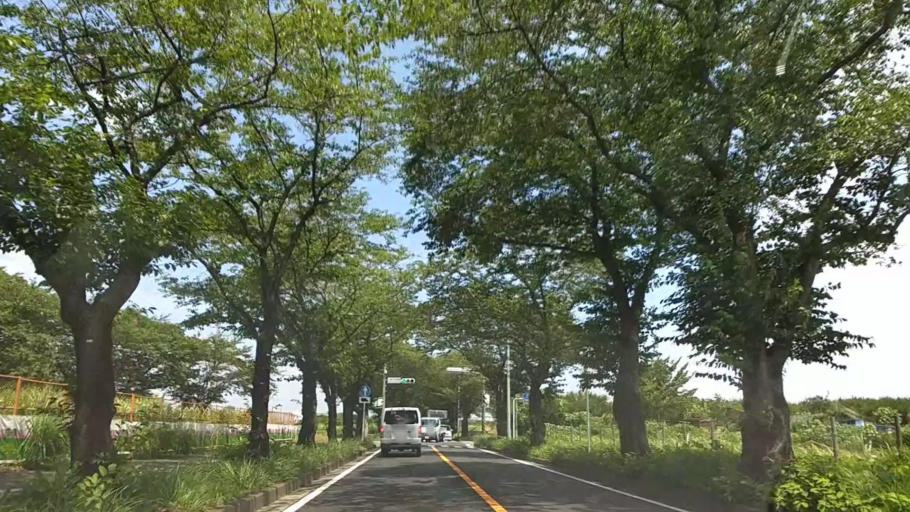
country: JP
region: Kanagawa
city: Minami-rinkan
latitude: 35.4892
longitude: 139.4803
